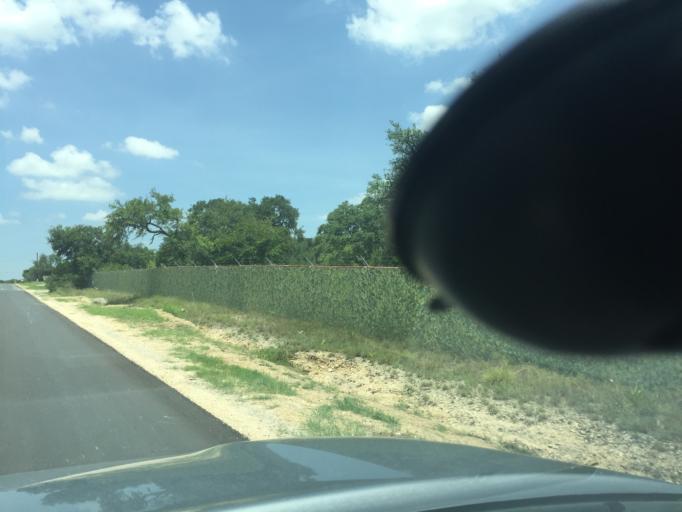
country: US
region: Texas
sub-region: Bexar County
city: Timberwood Park
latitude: 29.6967
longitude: -98.4543
